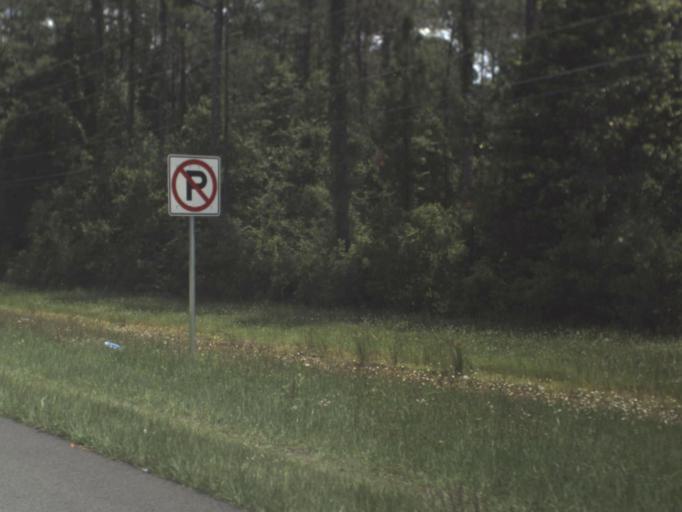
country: US
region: Florida
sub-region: Duval County
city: Baldwin
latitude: 30.2923
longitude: -81.9828
